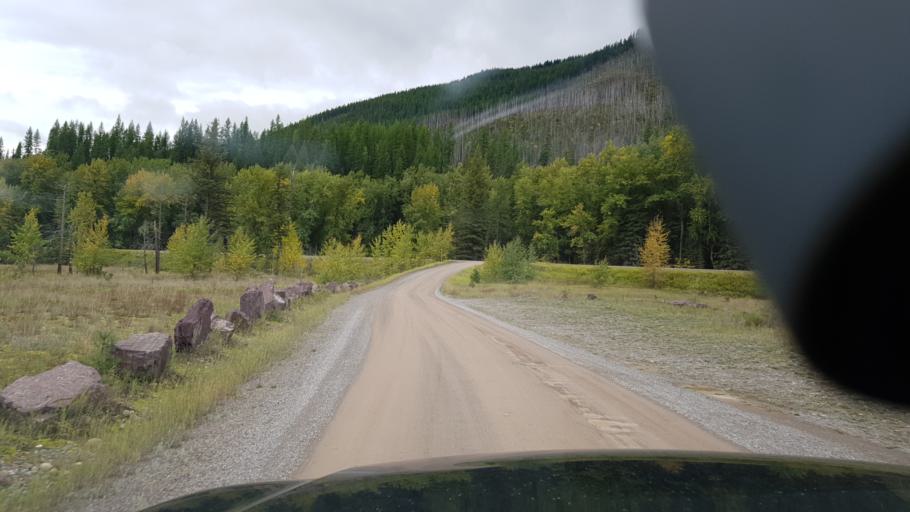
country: US
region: Montana
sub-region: Flathead County
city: Columbia Falls
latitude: 48.5685
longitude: -114.1309
